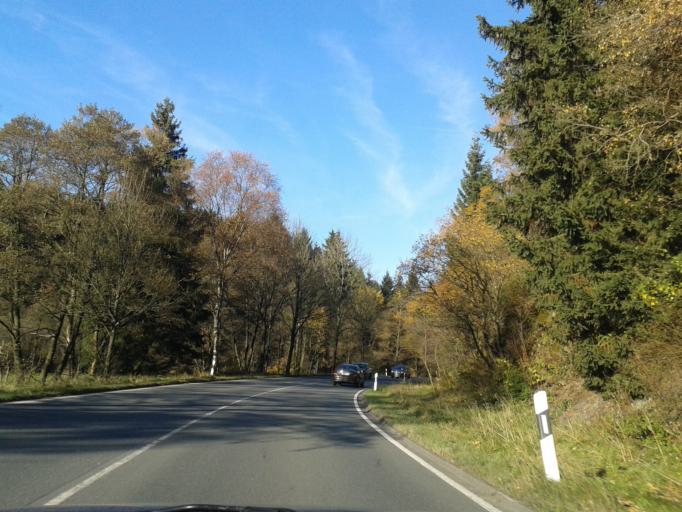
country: DE
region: North Rhine-Westphalia
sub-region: Regierungsbezirk Arnsberg
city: Bad Berleburg
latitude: 51.0180
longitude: 8.3723
